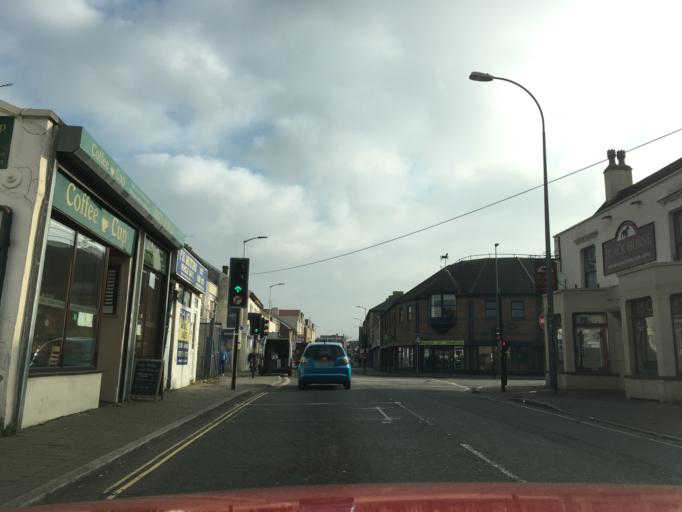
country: GB
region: England
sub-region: South Gloucestershire
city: Kingswood
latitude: 51.4631
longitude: -2.5126
